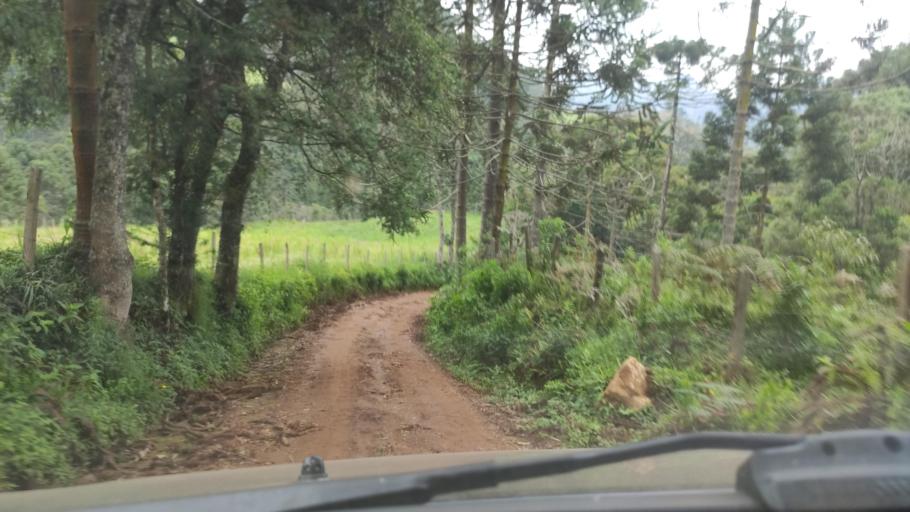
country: BR
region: Minas Gerais
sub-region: Paraisopolis
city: Paraisopolis
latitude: -22.7231
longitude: -45.8446
